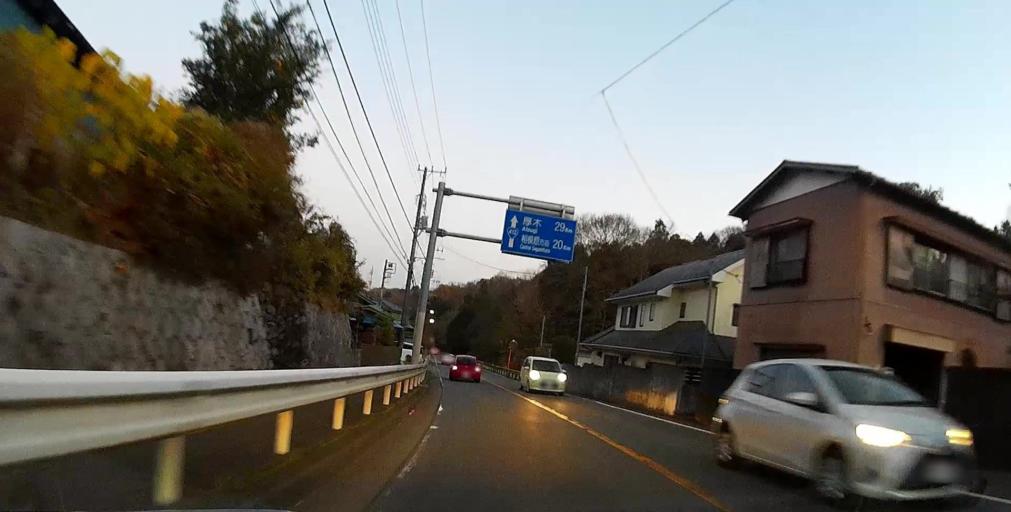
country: JP
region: Yamanashi
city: Uenohara
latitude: 35.6005
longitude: 139.2006
